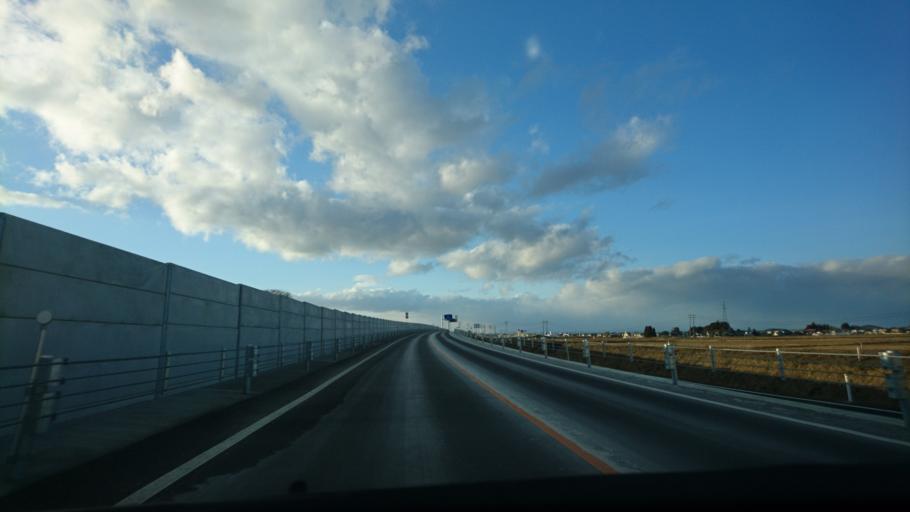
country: JP
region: Miyagi
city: Wakuya
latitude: 38.6884
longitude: 141.2230
